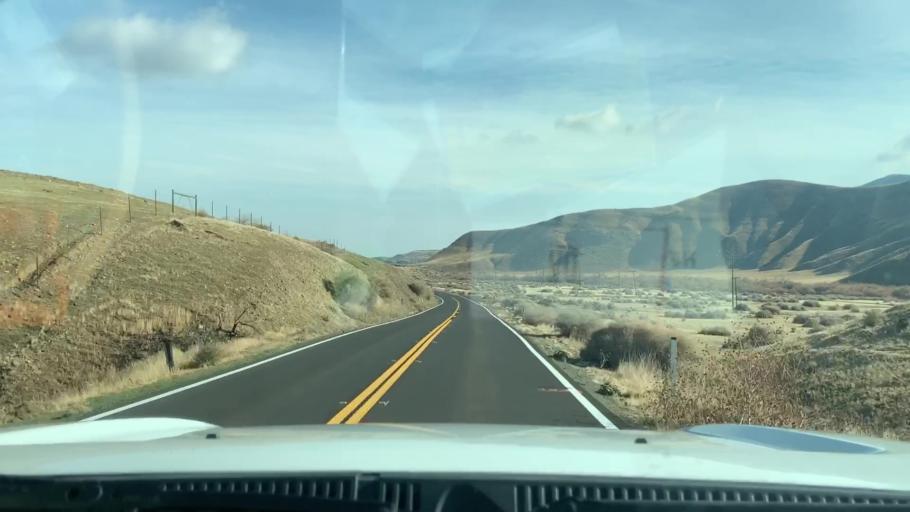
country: US
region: California
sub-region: Fresno County
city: Coalinga
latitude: 36.1017
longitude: -120.4120
